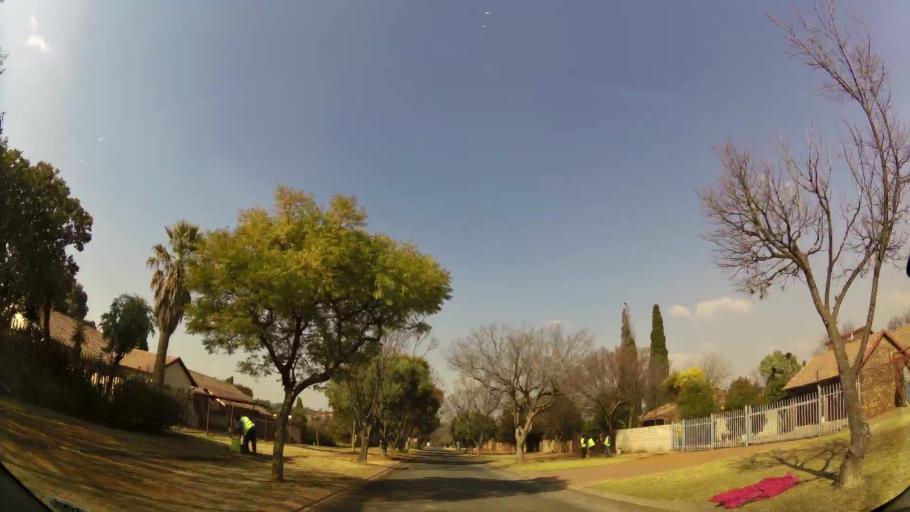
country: ZA
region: Gauteng
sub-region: Ekurhuleni Metropolitan Municipality
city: Benoni
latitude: -26.1574
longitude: 28.2839
